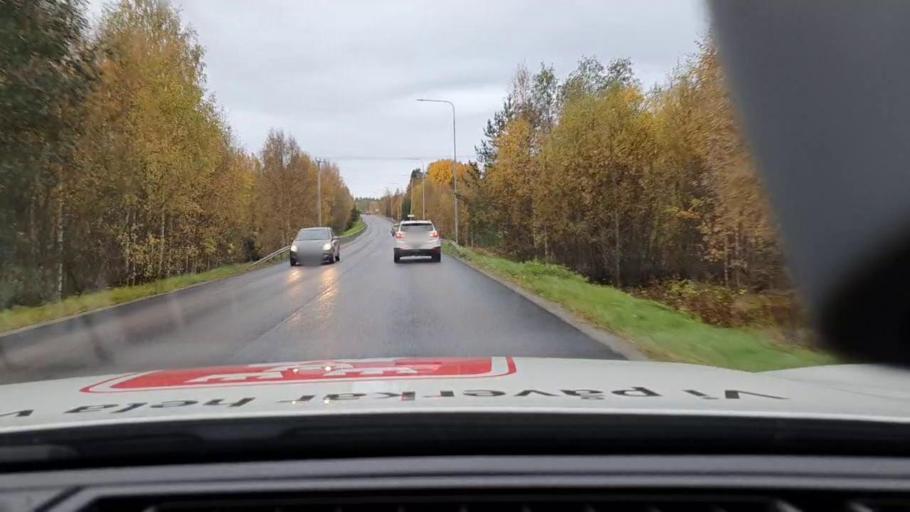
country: SE
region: Norrbotten
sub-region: Bodens Kommun
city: Saevast
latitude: 65.7666
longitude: 21.7393
